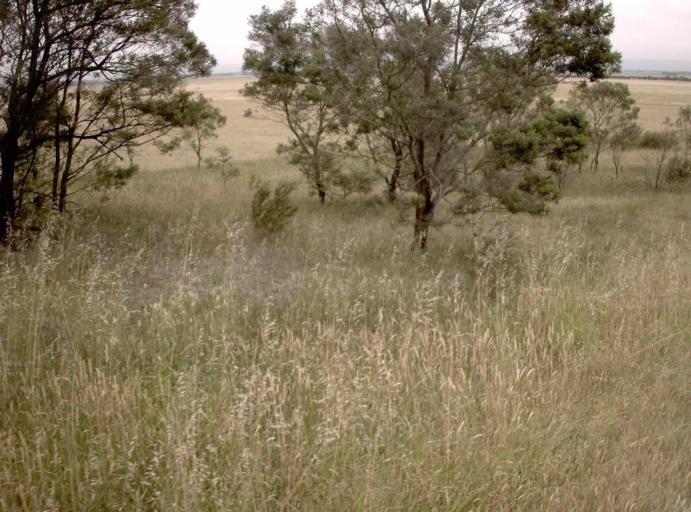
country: AU
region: Victoria
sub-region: Wellington
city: Heyfield
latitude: -38.1238
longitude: 146.7822
